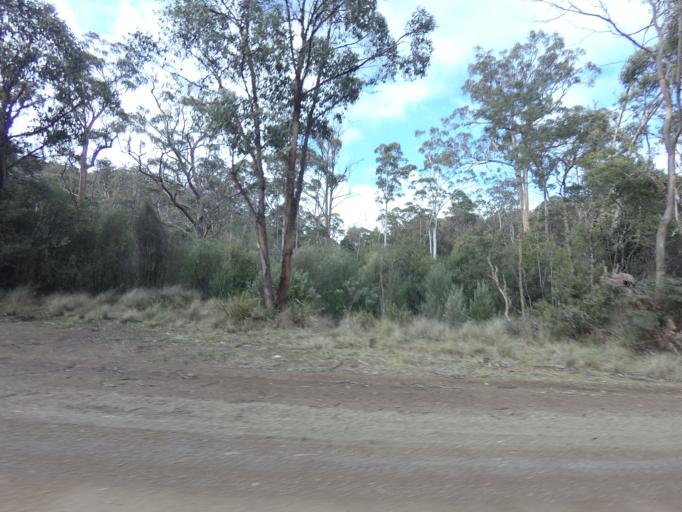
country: AU
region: Tasmania
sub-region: Derwent Valley
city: New Norfolk
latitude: -42.7459
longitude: 146.8663
